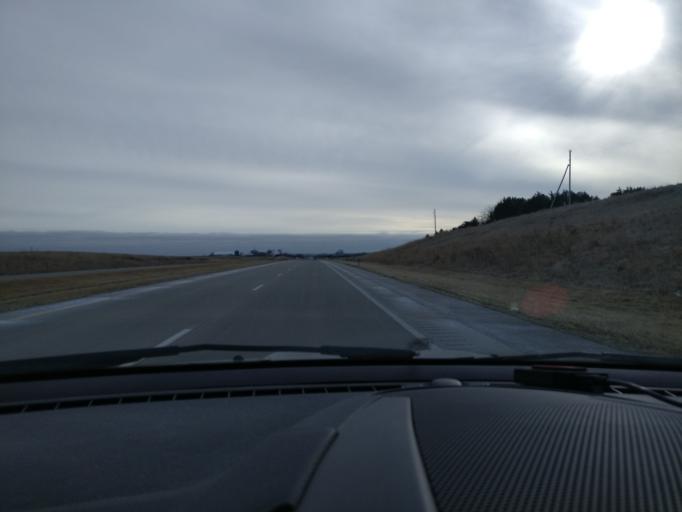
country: US
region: Nebraska
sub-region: Saunders County
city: Wahoo
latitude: 41.0866
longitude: -96.6402
